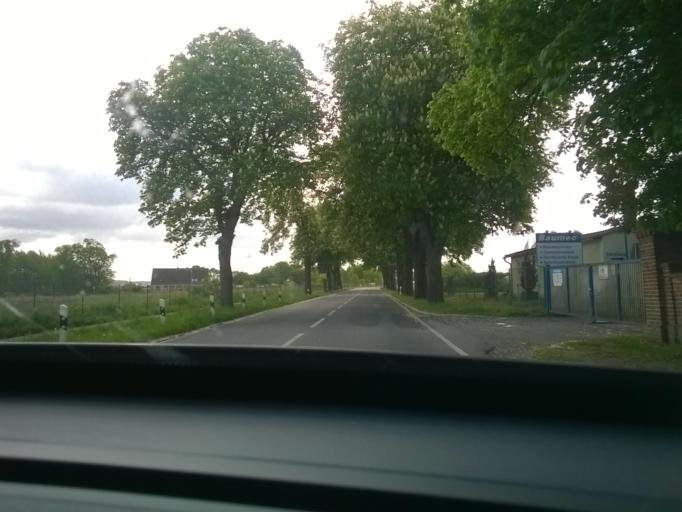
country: DE
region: Brandenburg
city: Wittstock
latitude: 53.1480
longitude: 12.4888
